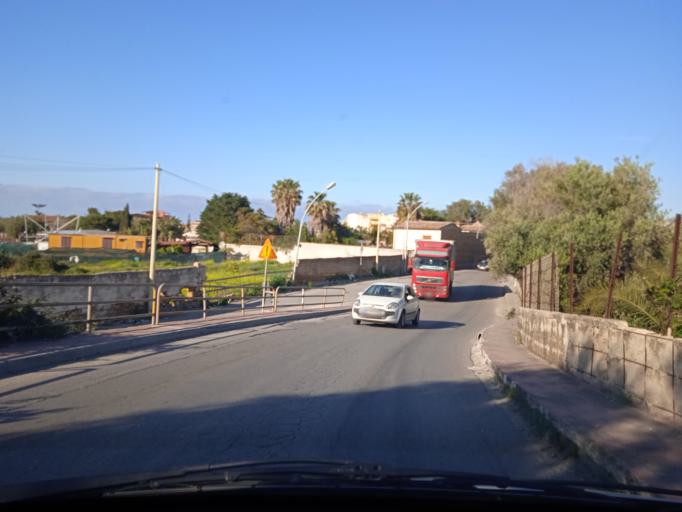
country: IT
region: Sicily
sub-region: Palermo
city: Villabate
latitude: 38.0871
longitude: 13.4500
